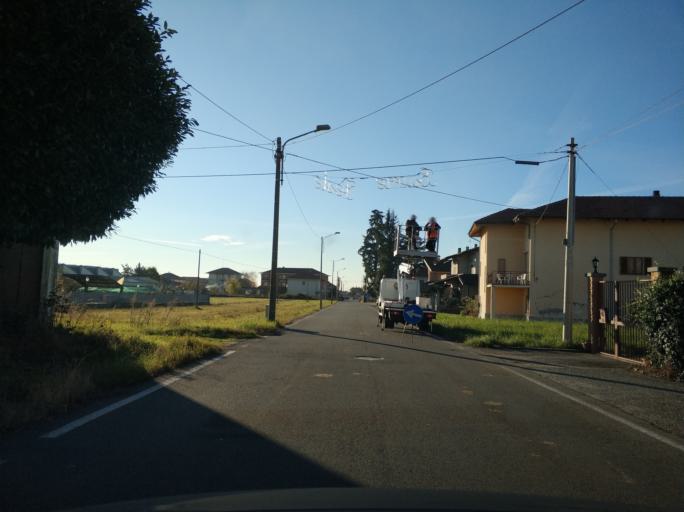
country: IT
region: Piedmont
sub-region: Provincia di Torino
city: Grosso
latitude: 45.2519
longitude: 7.5562
